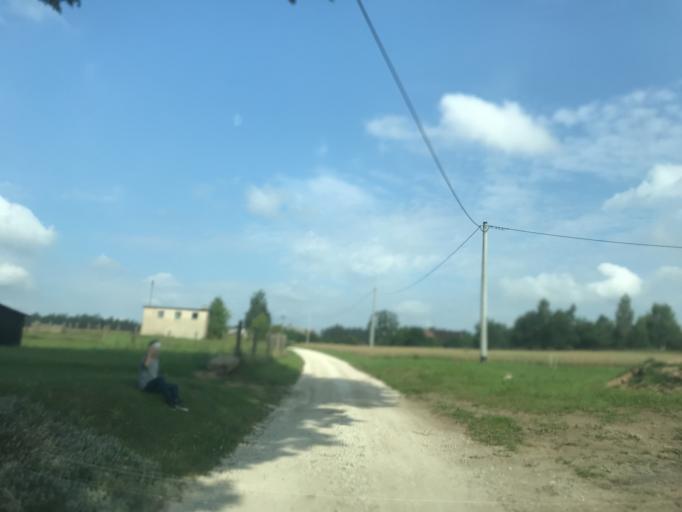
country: PL
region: Warmian-Masurian Voivodeship
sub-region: Powiat nowomiejski
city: Kurzetnik
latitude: 53.3485
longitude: 19.4836
